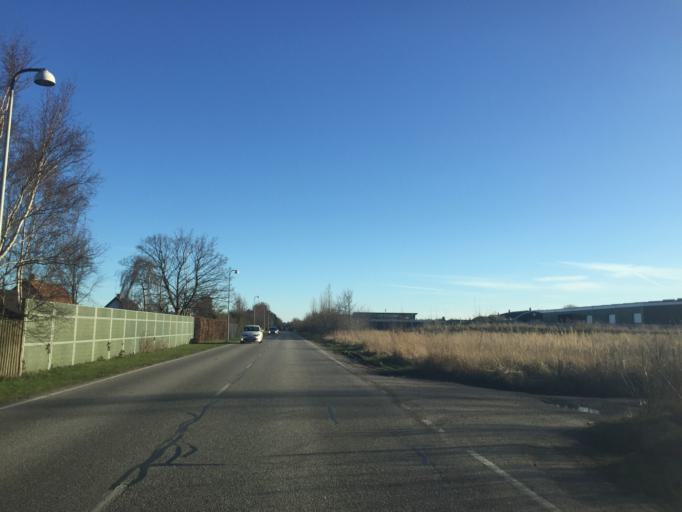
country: DK
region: Capital Region
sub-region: Dragor Kommune
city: Dragor
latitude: 55.6044
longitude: 12.6615
